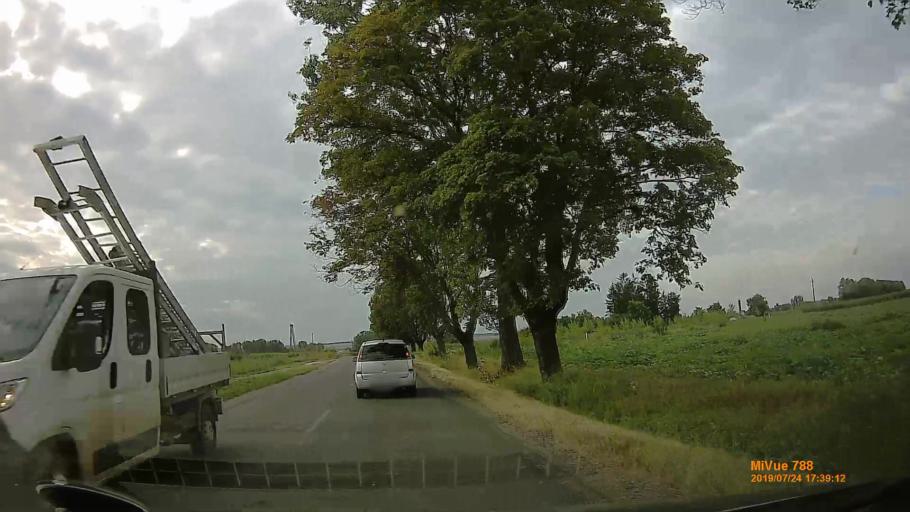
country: HU
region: Borsod-Abauj-Zemplen
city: Encs
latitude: 48.3247
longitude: 21.1476
